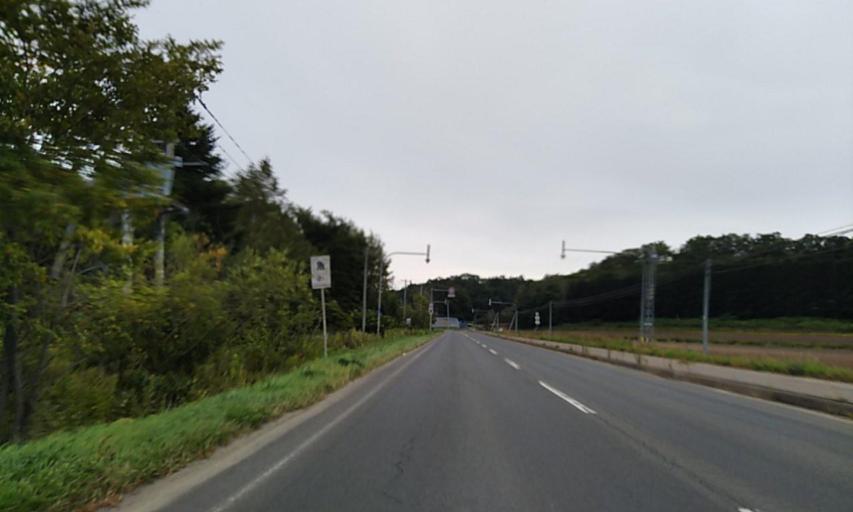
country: JP
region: Hokkaido
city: Bihoro
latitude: 43.7380
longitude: 144.0463
